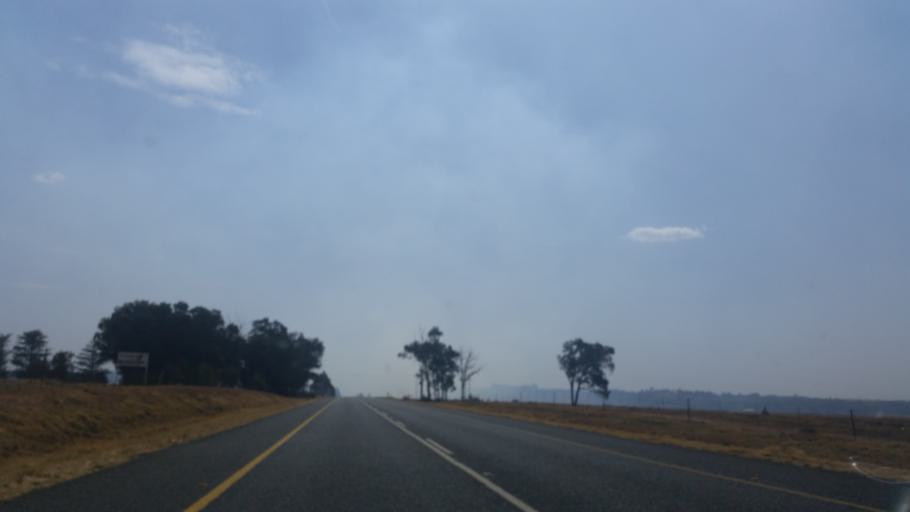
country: ZA
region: Orange Free State
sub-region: Thabo Mofutsanyana District Municipality
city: Bethlehem
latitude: -28.2706
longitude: 28.3696
